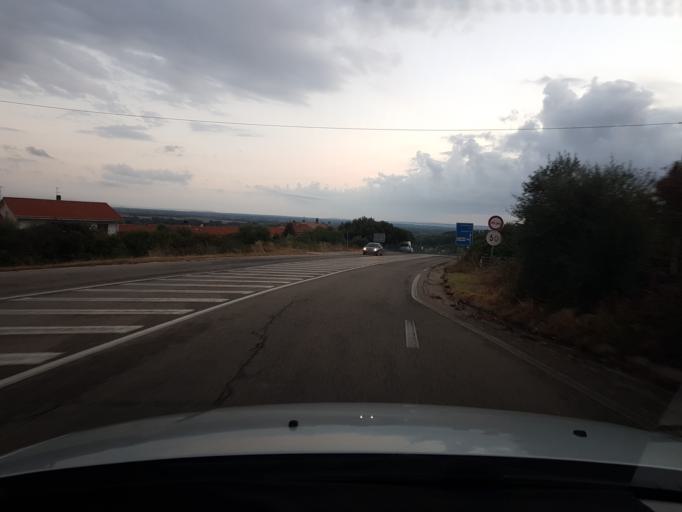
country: IT
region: Sardinia
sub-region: Provincia di Oristano
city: Milis
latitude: 40.0554
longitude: 8.6369
